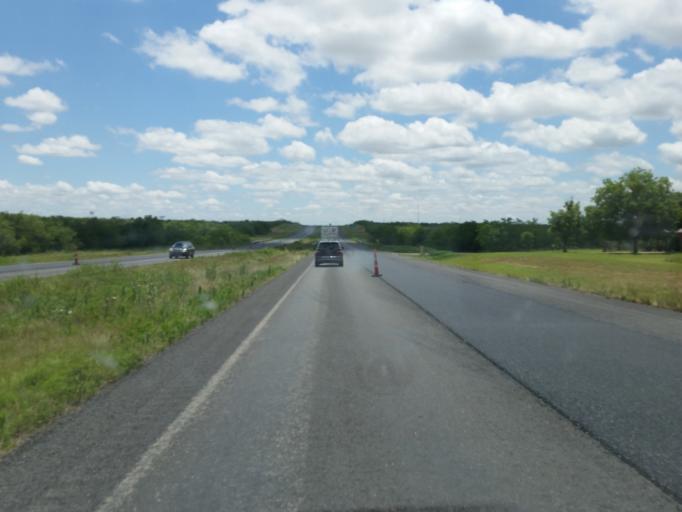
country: US
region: Texas
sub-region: Scurry County
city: Snyder
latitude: 32.7643
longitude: -100.9342
